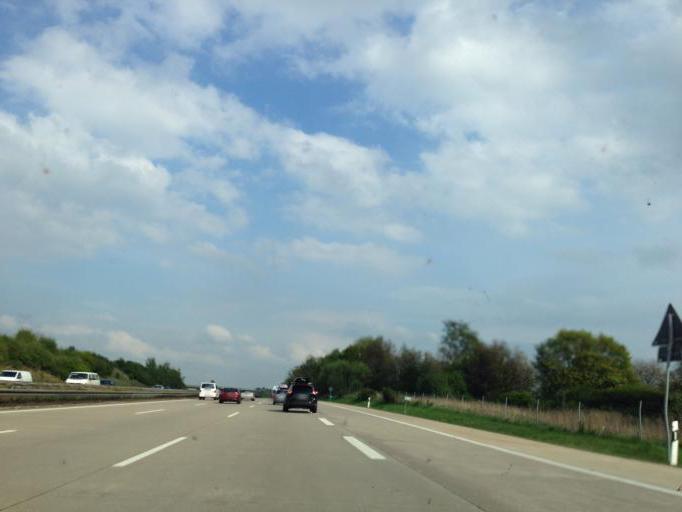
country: DE
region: Saxony
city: Reinsberg
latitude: 51.0587
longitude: 13.3881
